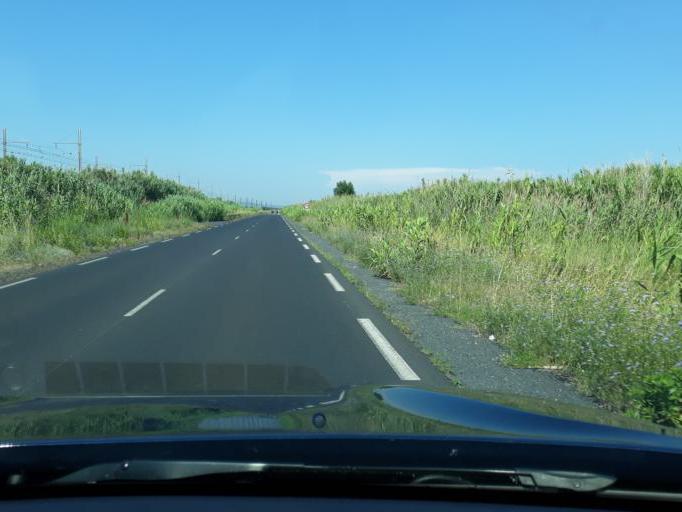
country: FR
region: Languedoc-Roussillon
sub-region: Departement de l'Herault
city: Marseillan
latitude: 43.3457
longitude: 3.5817
